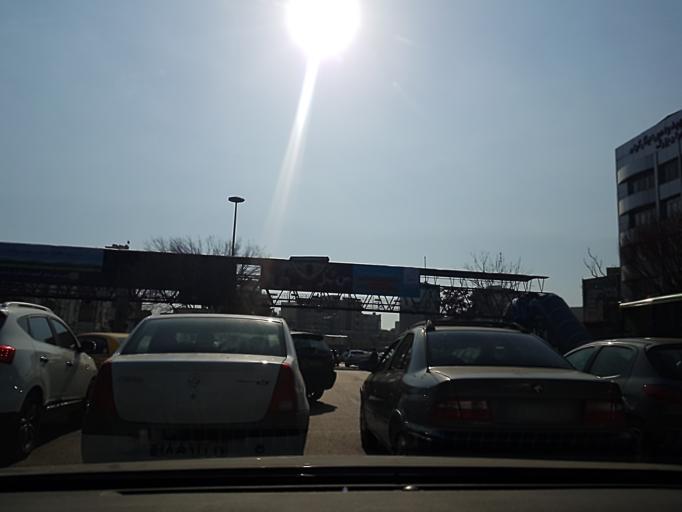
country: IR
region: Tehran
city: Tehran
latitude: 35.7173
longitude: 51.4268
